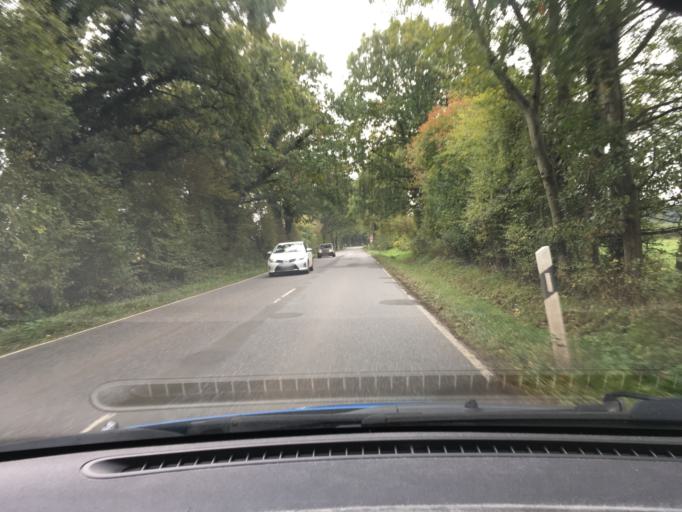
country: DE
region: Schleswig-Holstein
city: Klein Ronnau
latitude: 53.9827
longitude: 10.3124
